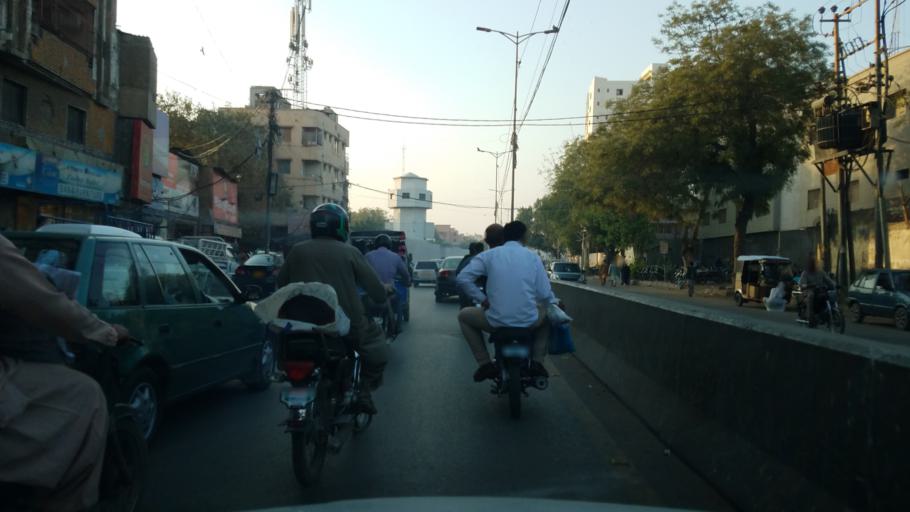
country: PK
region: Sindh
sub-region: Karachi District
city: Karachi
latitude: 24.8678
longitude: 67.0234
